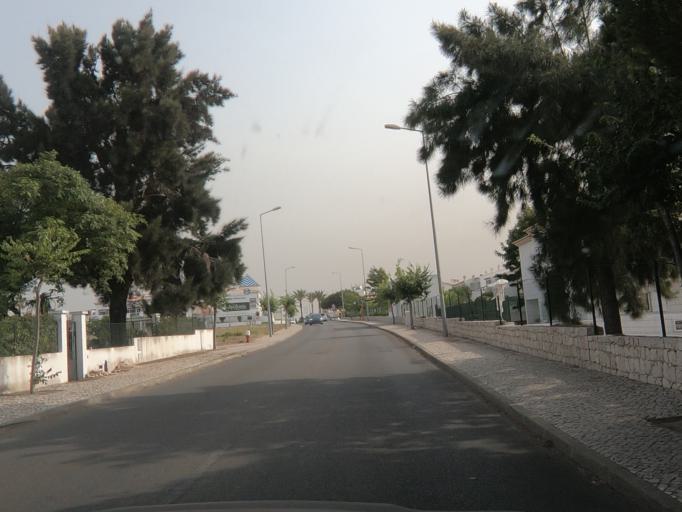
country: PT
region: Faro
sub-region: Albufeira
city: Guia
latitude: 37.0851
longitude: -8.3097
